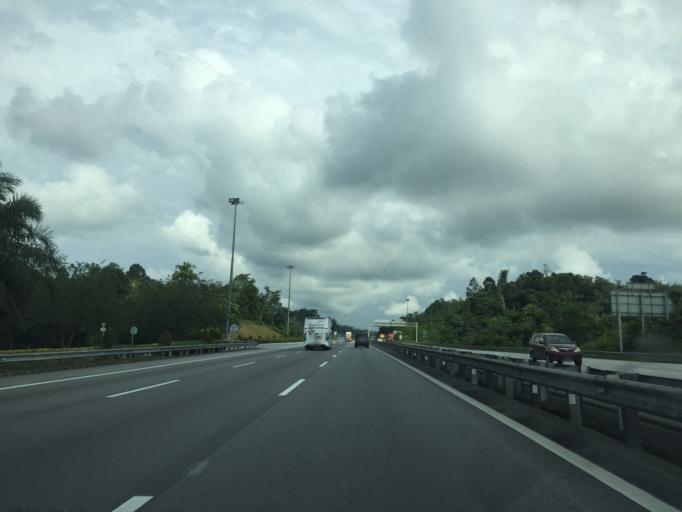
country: MY
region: Selangor
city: Batang Berjuntai
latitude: 3.5803
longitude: 101.5241
